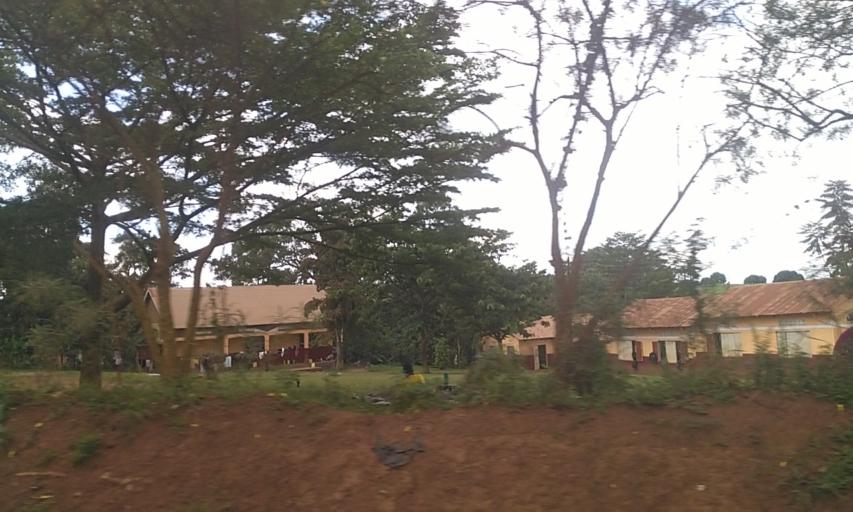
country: UG
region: Central Region
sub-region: Wakiso District
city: Wakiso
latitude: 0.3528
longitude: 32.4702
